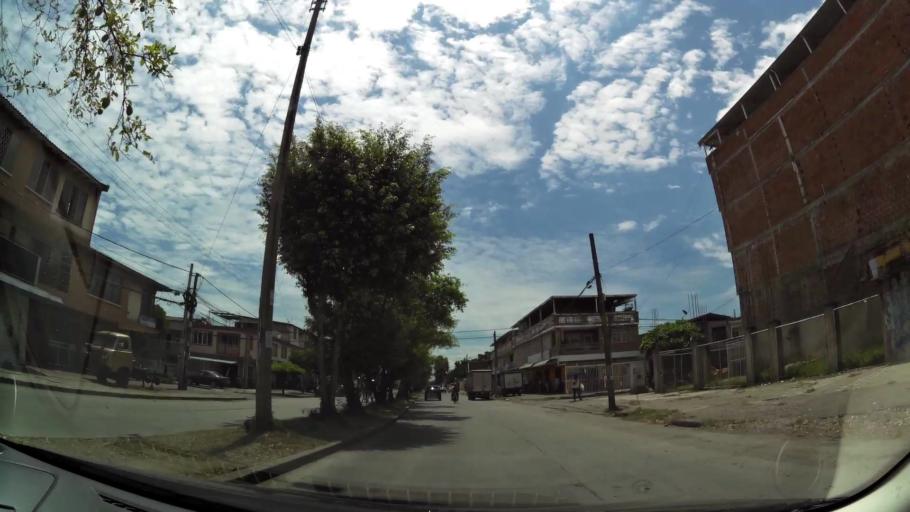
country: CO
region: Valle del Cauca
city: Cali
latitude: 3.4425
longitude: -76.4996
